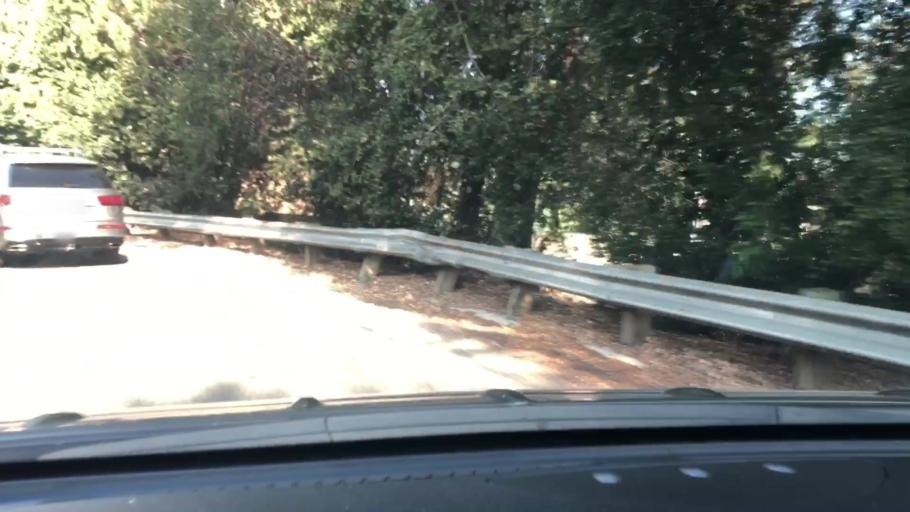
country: US
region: California
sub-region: Santa Clara County
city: Los Gatos
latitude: 37.2510
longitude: -121.9607
